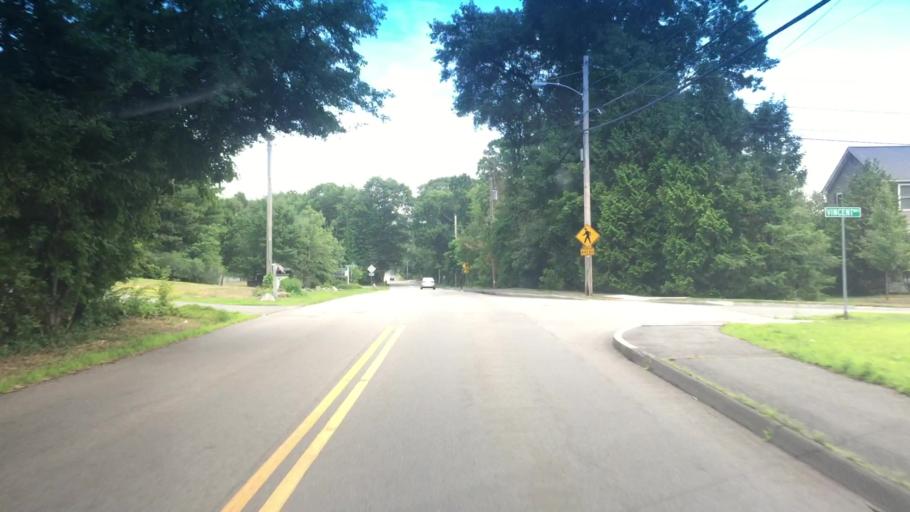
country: US
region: Massachusetts
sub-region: Norfolk County
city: Medway
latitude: 42.1235
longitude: -71.3981
